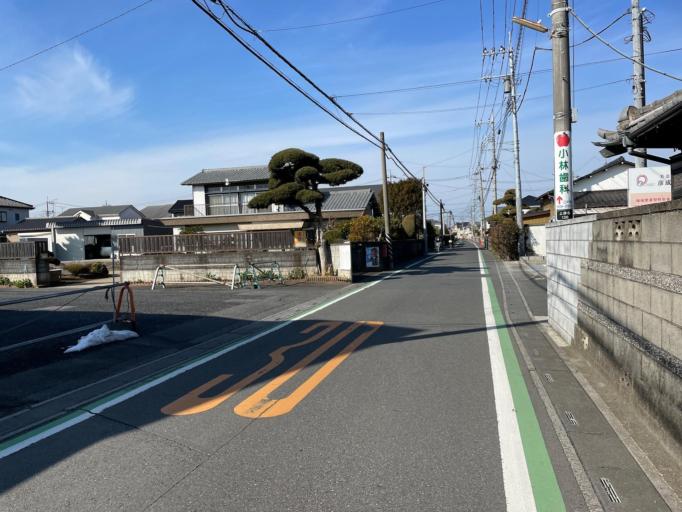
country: JP
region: Saitama
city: Yashio-shi
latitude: 35.8497
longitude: 139.8452
